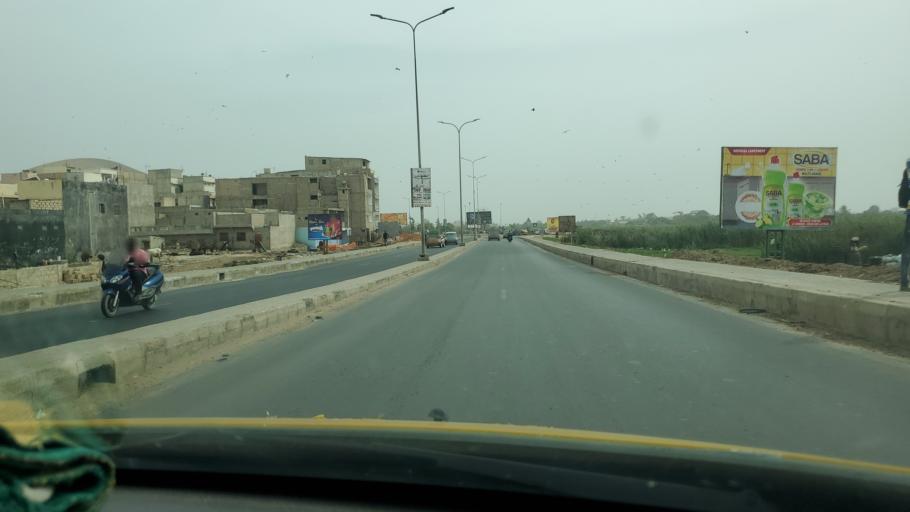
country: SN
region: Dakar
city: Pikine
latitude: 14.7661
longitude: -17.3991
